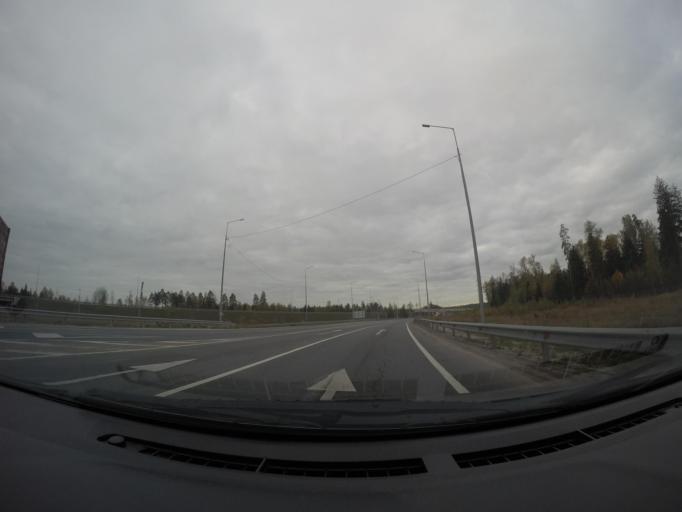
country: RU
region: Moskovskaya
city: Fryazevo
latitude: 55.6981
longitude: 38.4344
